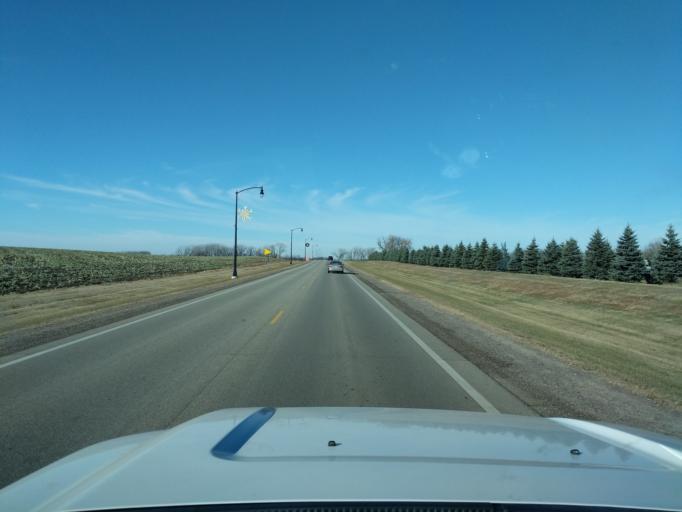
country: US
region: Minnesota
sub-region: Yellow Medicine County
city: Granite Falls
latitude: 44.7642
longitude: -95.5298
